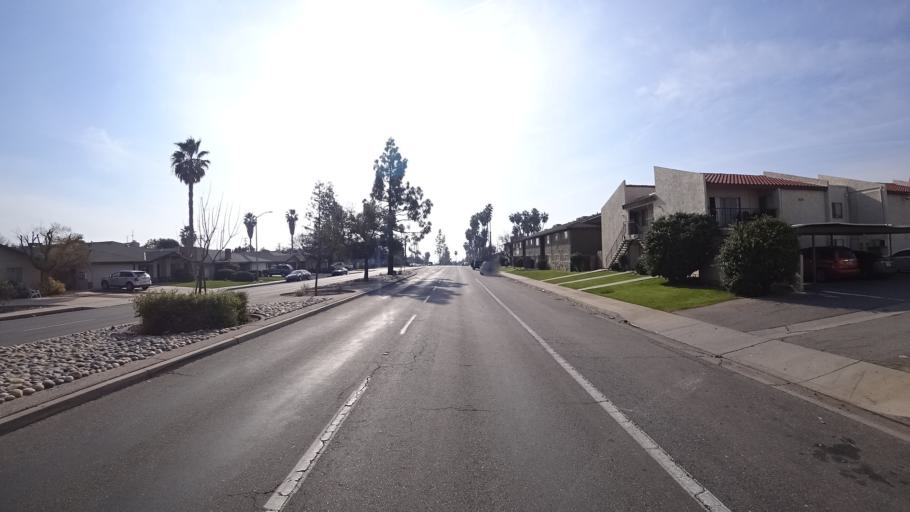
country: US
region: California
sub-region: Kern County
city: Oildale
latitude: 35.4089
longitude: -118.9477
